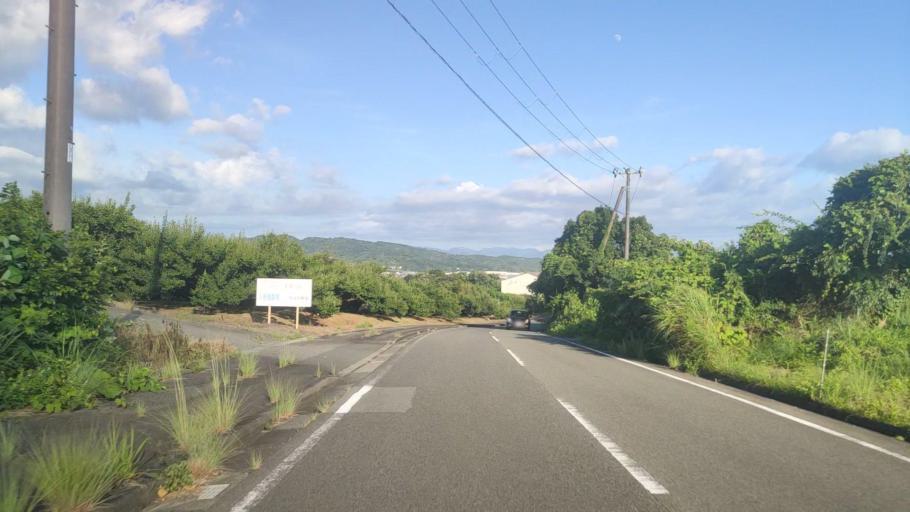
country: JP
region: Wakayama
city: Tanabe
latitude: 33.7775
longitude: 135.3030
